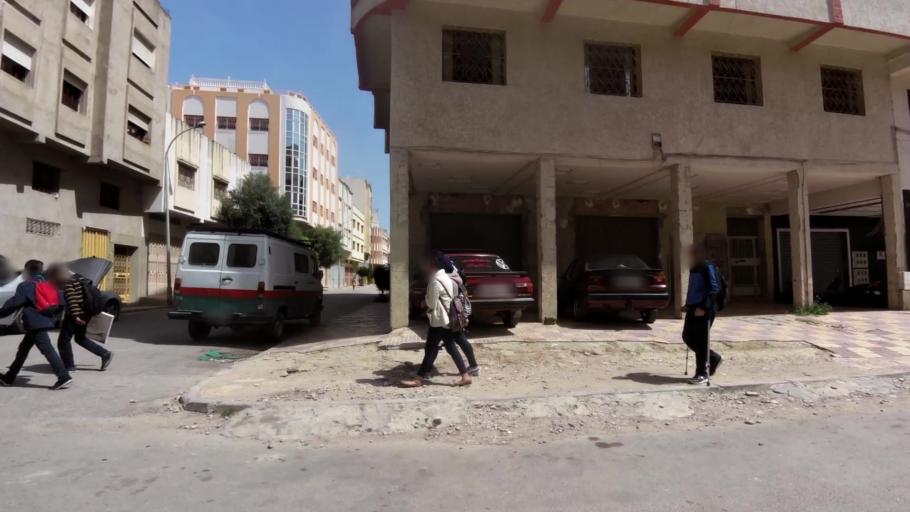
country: MA
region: Tanger-Tetouan
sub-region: Tanger-Assilah
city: Tangier
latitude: 35.7567
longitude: -5.8404
